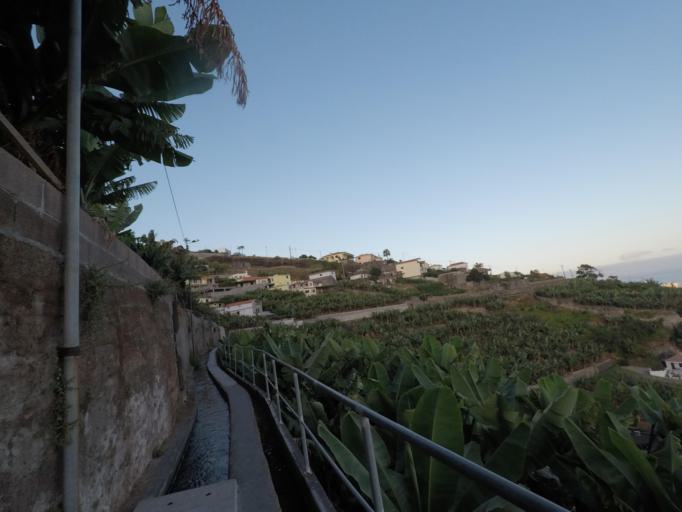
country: PT
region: Madeira
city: Camara de Lobos
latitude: 32.6459
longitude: -16.9560
